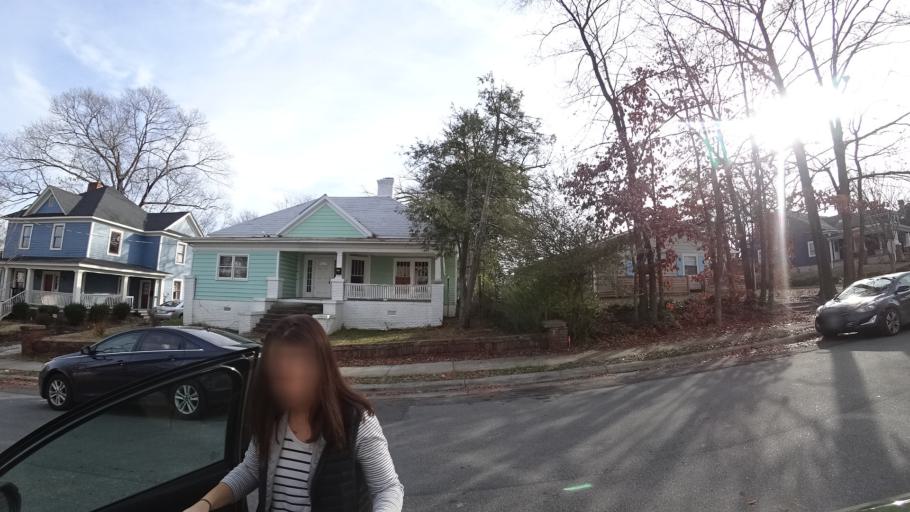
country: US
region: North Carolina
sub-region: Durham County
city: Durham
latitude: 35.9964
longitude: -78.8936
